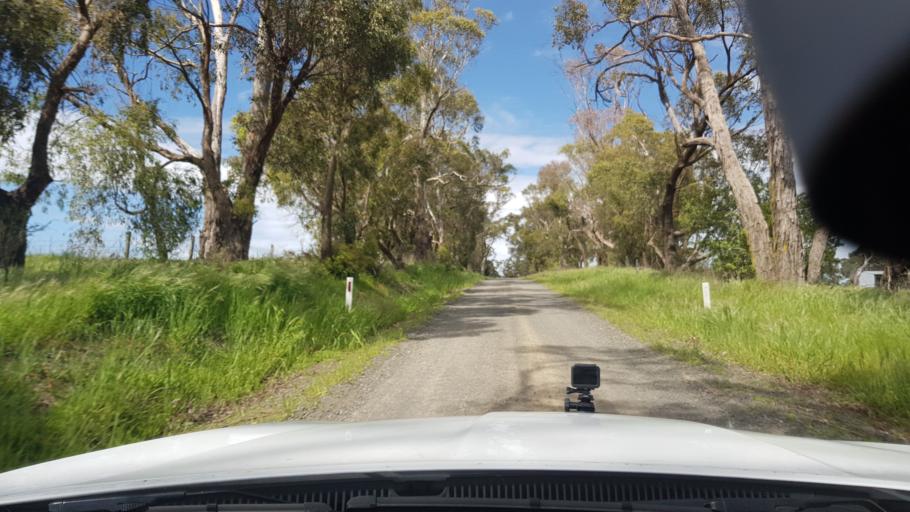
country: AU
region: Victoria
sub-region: Latrobe
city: Moe
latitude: -38.1522
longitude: 146.1369
